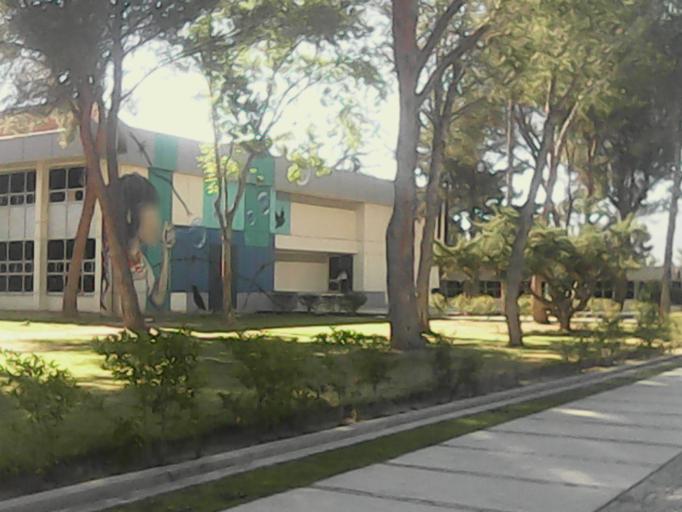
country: MX
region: Hidalgo
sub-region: Mineral de la Reforma
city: Carboneras
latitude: 20.0940
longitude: -98.7111
